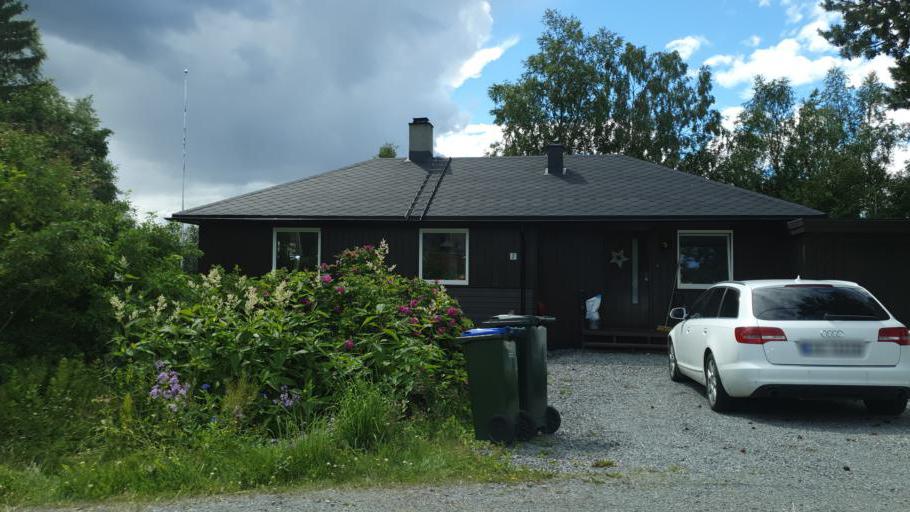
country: NO
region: Sor-Trondelag
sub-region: Rennebu
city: Berkak
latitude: 62.8328
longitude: 10.0076
